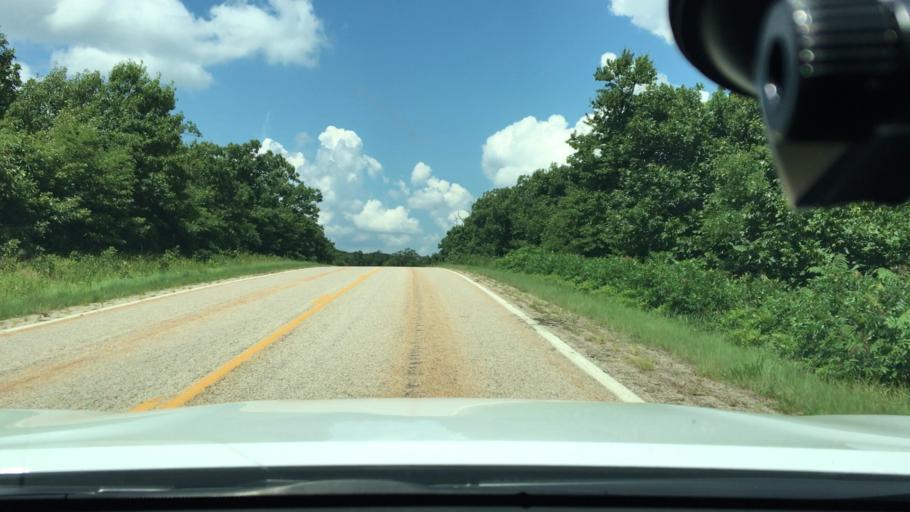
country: US
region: Arkansas
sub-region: Logan County
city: Paris
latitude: 35.1768
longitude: -93.6111
